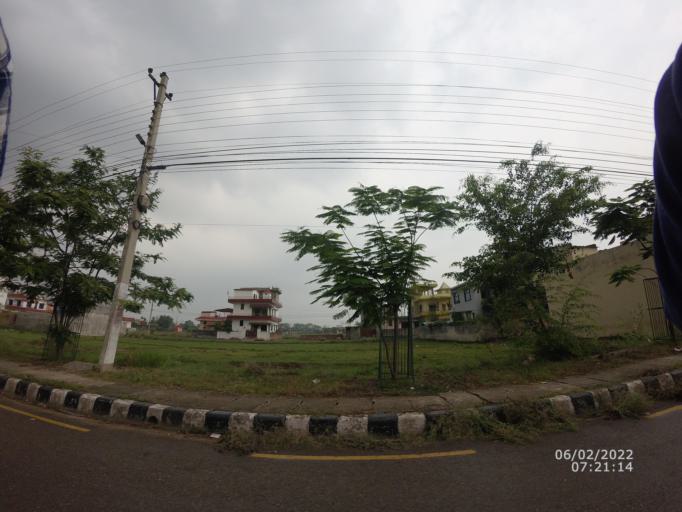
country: NP
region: Western Region
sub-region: Lumbini Zone
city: Bhairahawa
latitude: 27.4877
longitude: 83.4429
